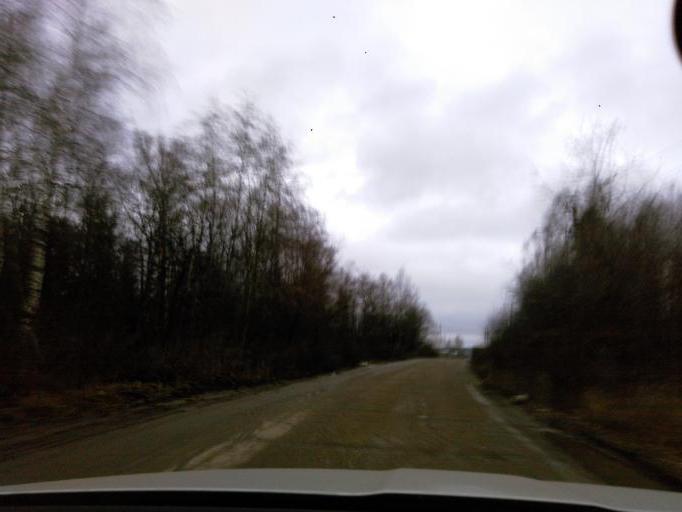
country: RU
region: Moskovskaya
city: Radumlya
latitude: 56.0574
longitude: 37.1277
